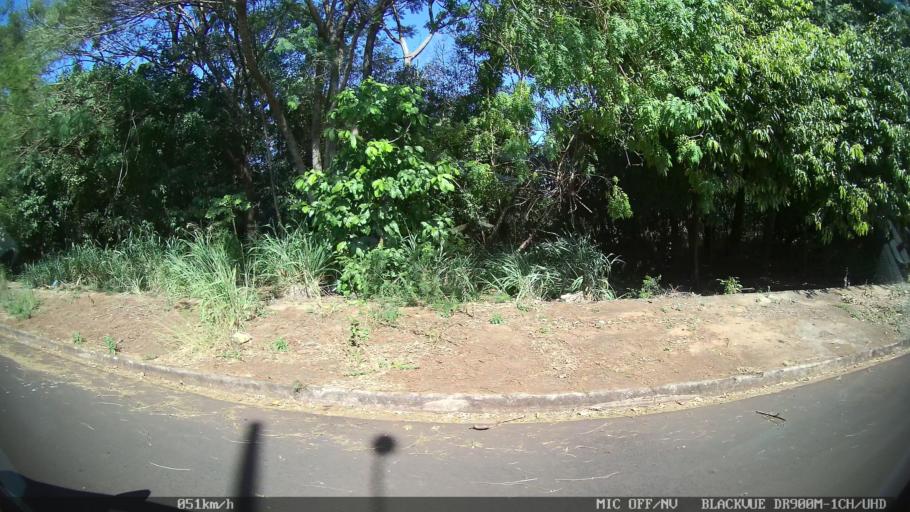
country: BR
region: Sao Paulo
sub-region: Batatais
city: Batatais
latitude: -20.8905
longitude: -47.5775
